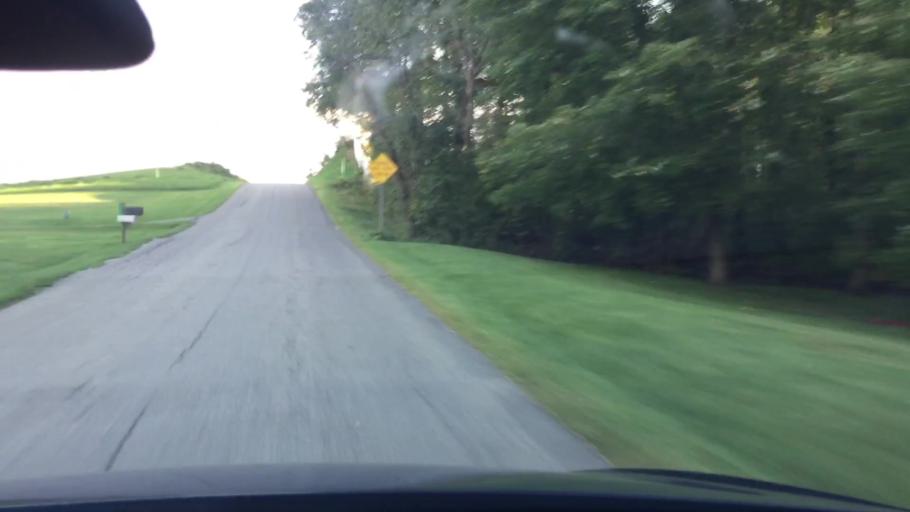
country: US
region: Pennsylvania
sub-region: Butler County
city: Nixon
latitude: 40.7624
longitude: -79.8854
